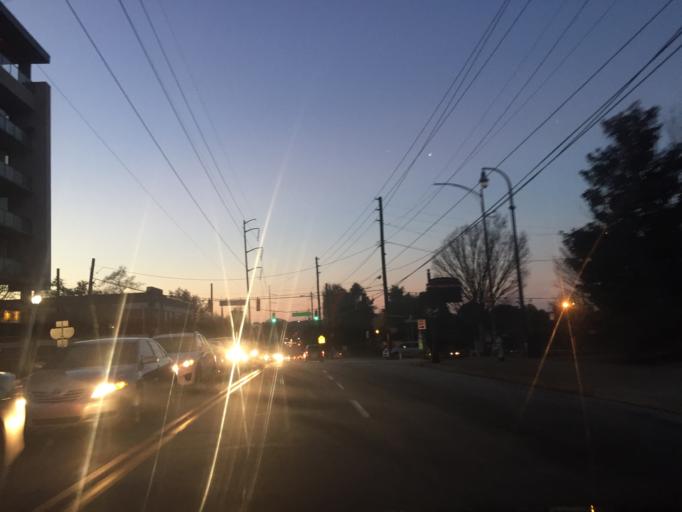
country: US
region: Georgia
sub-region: Fulton County
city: Atlanta
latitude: 33.7599
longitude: -84.3721
